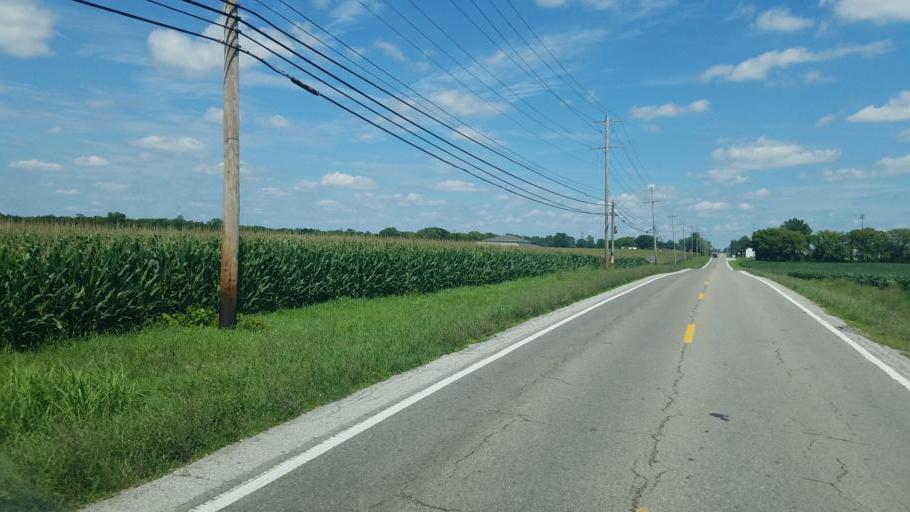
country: US
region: Ohio
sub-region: Franklin County
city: Obetz
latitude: 39.8626
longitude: -83.0005
